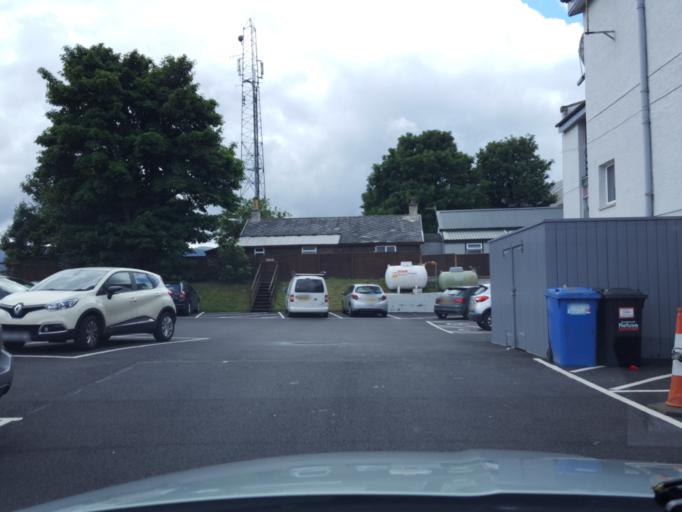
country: GB
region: Scotland
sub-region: Highland
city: Aviemore
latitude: 57.1924
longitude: -3.8281
